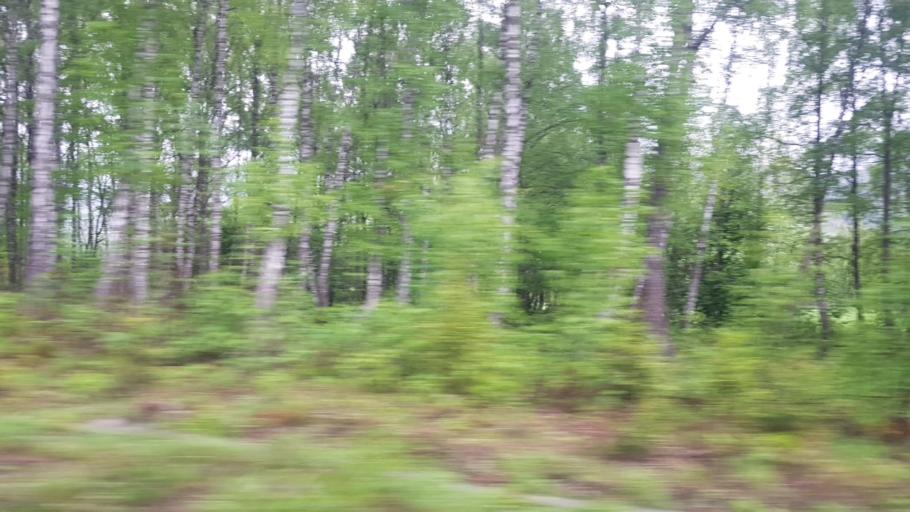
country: NO
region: Oppland
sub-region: Ringebu
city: Ringebu
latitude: 61.4210
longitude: 10.2161
